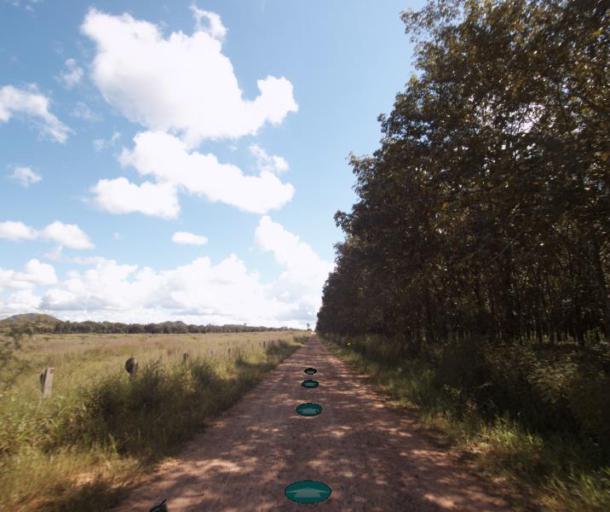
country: BR
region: Goias
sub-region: Pirenopolis
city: Pirenopolis
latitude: -15.7785
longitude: -49.0393
